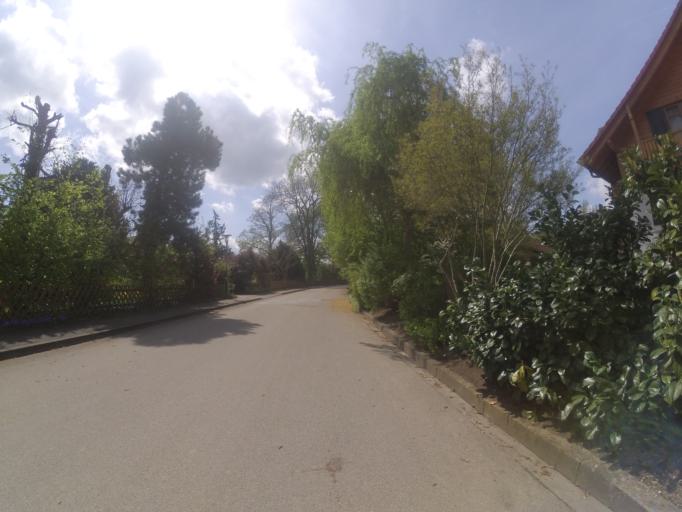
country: DE
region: Baden-Wuerttemberg
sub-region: Tuebingen Region
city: Opfingen
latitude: 48.2687
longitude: 9.8265
